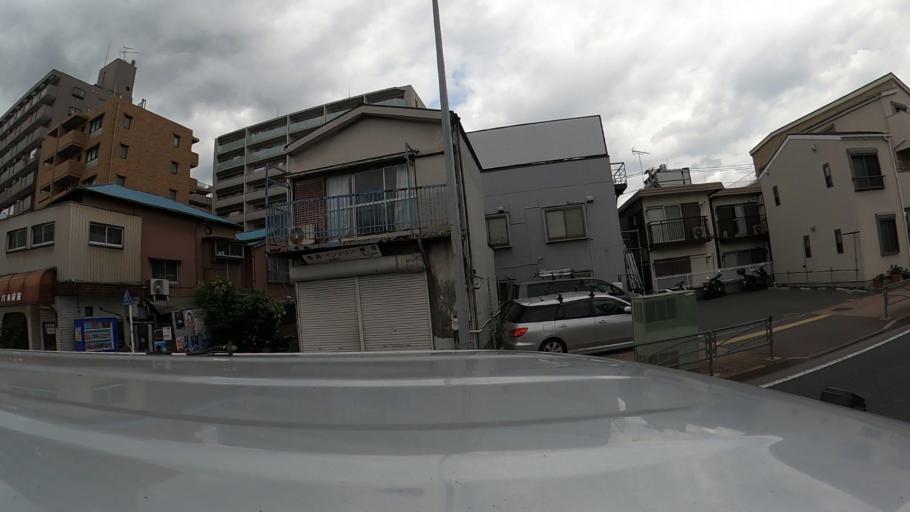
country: JP
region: Kanagawa
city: Yokohama
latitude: 35.4933
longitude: 139.6666
